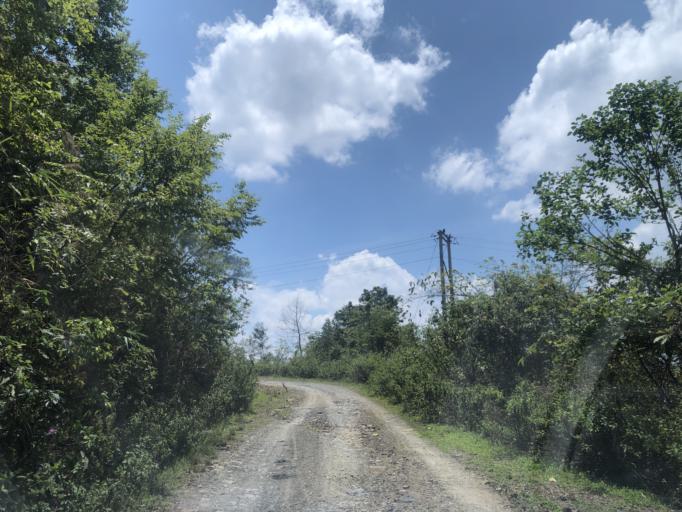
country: LA
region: Phongsali
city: Phongsali
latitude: 21.4422
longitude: 102.1635
